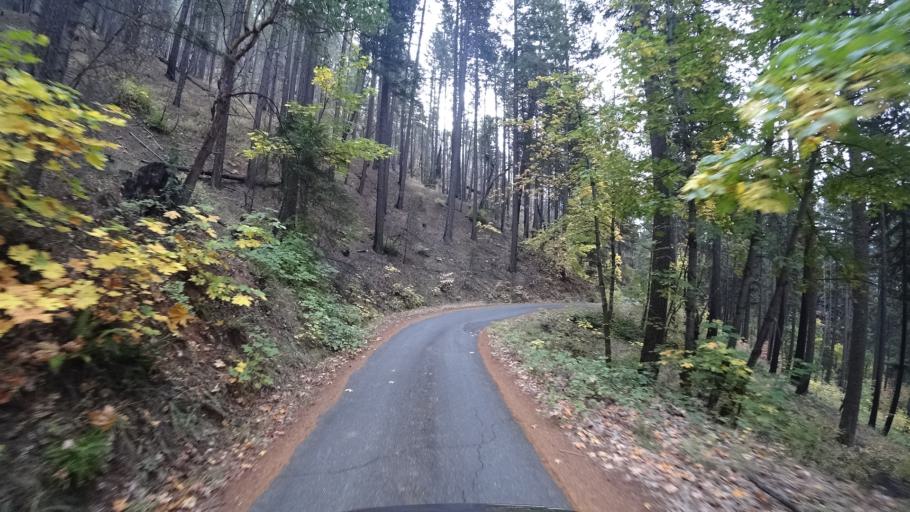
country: US
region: California
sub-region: Siskiyou County
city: Happy Camp
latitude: 41.8177
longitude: -123.3324
